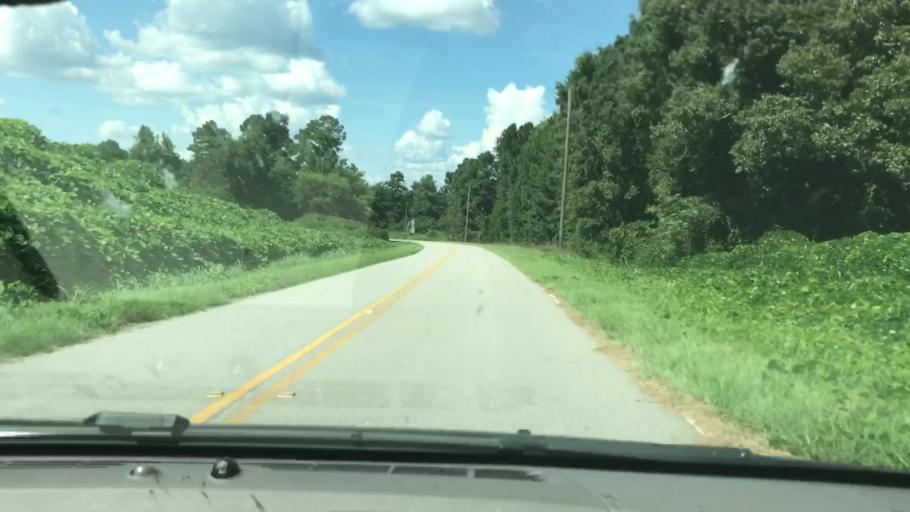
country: US
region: Georgia
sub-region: Troup County
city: La Grange
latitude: 33.0840
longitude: -85.1289
